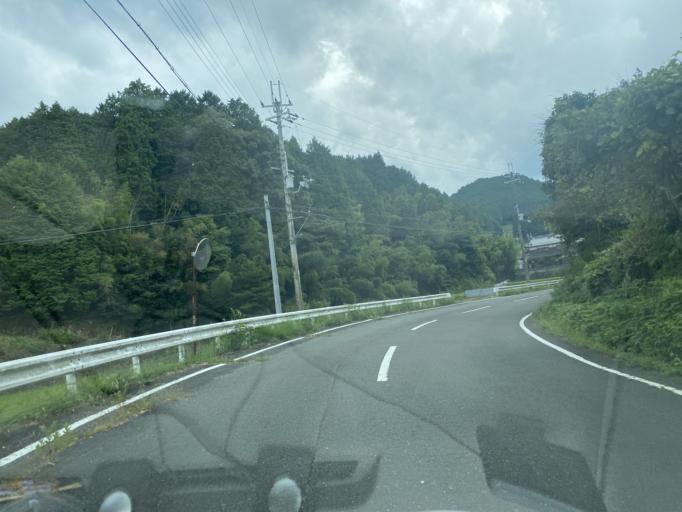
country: JP
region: Nara
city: Nara-shi
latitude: 34.6898
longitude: 135.9020
